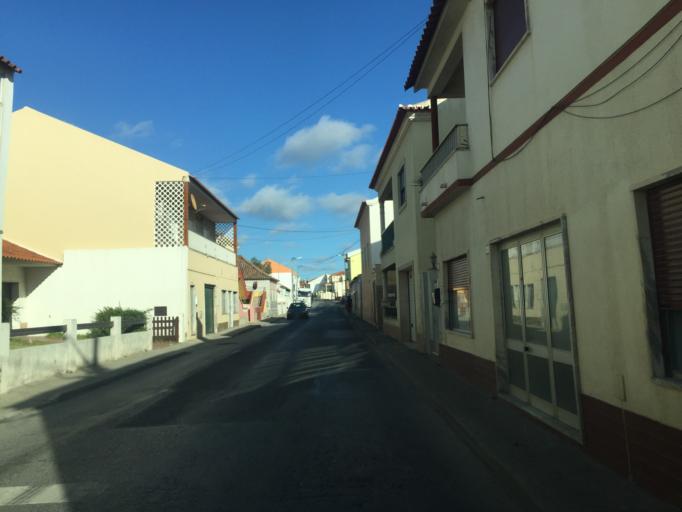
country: PT
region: Lisbon
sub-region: Torres Vedras
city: A dos Cunhados
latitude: 39.1498
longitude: -9.2963
